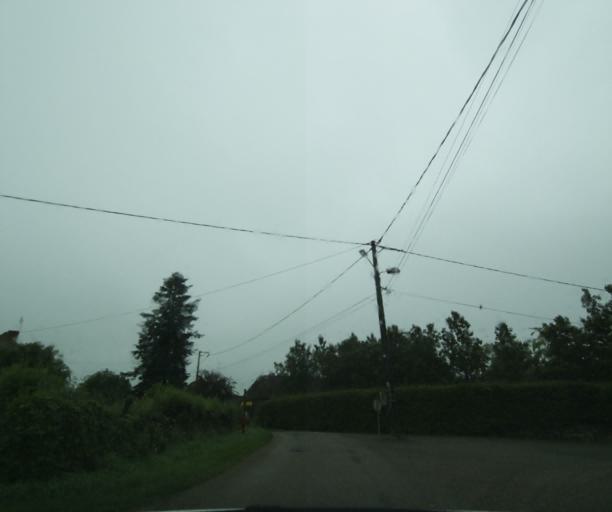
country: FR
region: Bourgogne
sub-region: Departement de Saone-et-Loire
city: Charolles
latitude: 46.3972
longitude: 4.2138
